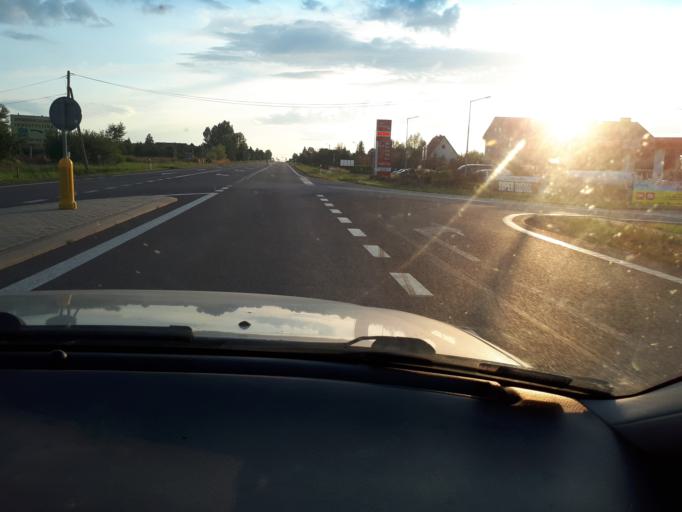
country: PL
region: Subcarpathian Voivodeship
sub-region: Powiat ropczycko-sedziszowski
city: Iwierzyce
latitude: 50.0707
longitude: 21.7675
